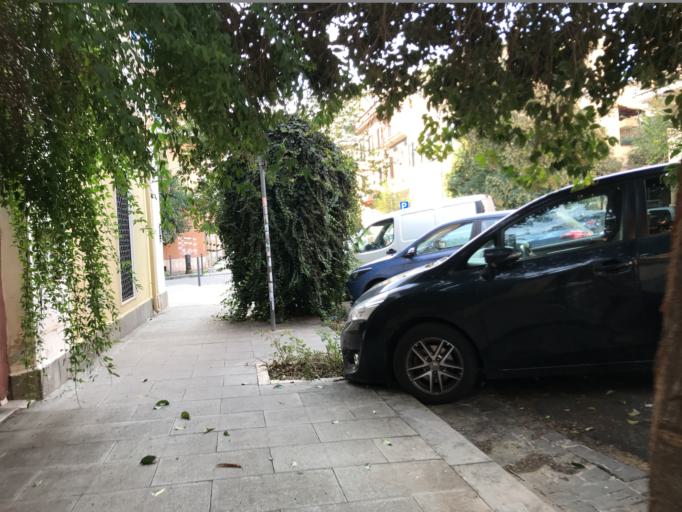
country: IT
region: Latium
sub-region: Citta metropolitana di Roma Capitale
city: Rome
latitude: 41.9104
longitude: 12.5167
